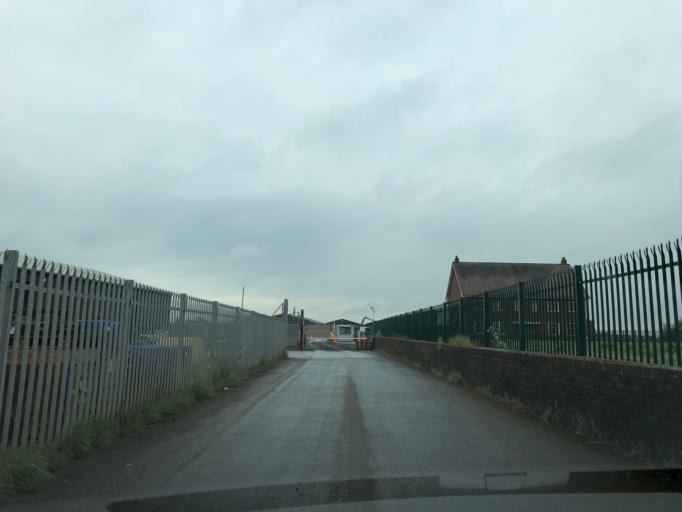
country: GB
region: England
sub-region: North Yorkshire
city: Thirsk
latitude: 54.2170
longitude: -1.4222
